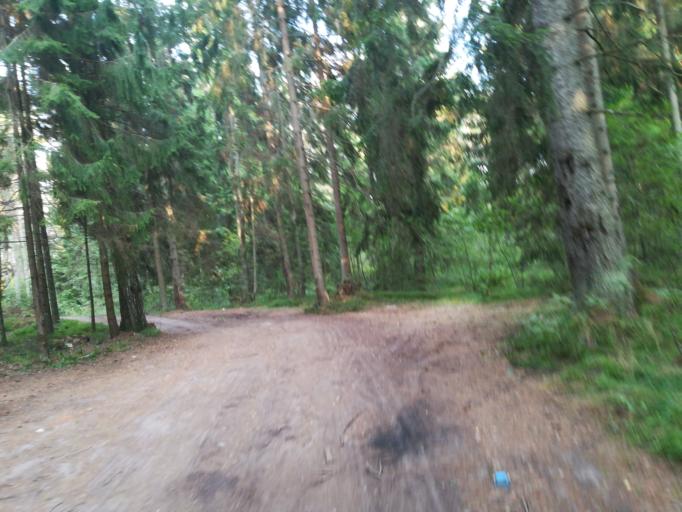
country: RU
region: Leningrad
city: Ust'-Luga
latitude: 59.6782
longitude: 28.2375
